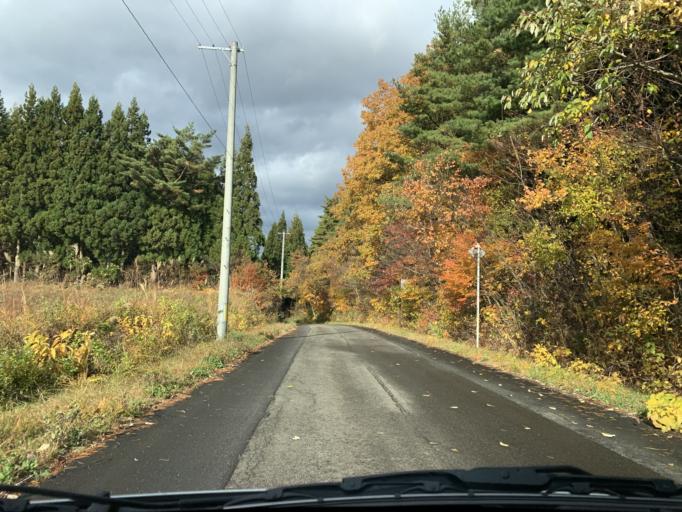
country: JP
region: Iwate
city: Mizusawa
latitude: 39.1111
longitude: 140.9731
